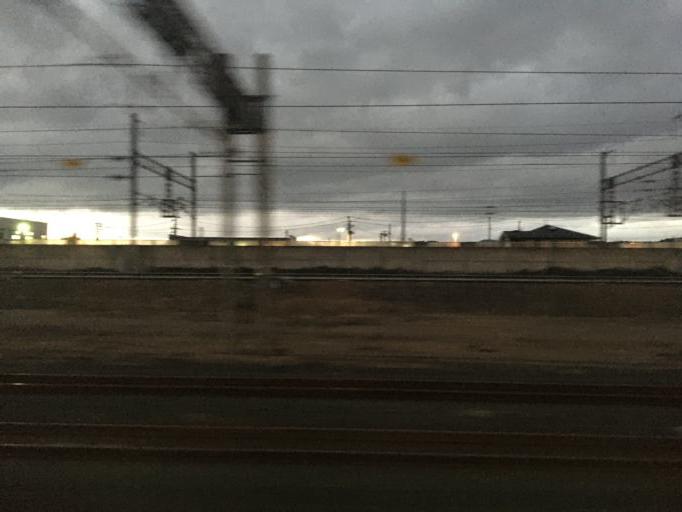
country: JP
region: Aomori
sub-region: Hachinohe Shi
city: Uchimaru
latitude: 40.5117
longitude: 141.4339
